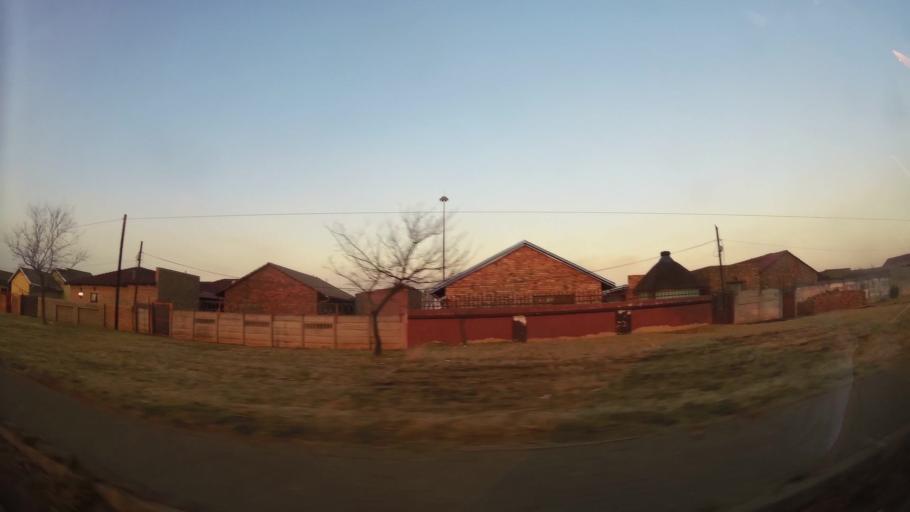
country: ZA
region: Gauteng
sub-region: Ekurhuleni Metropolitan Municipality
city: Springs
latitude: -26.2991
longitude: 28.4073
